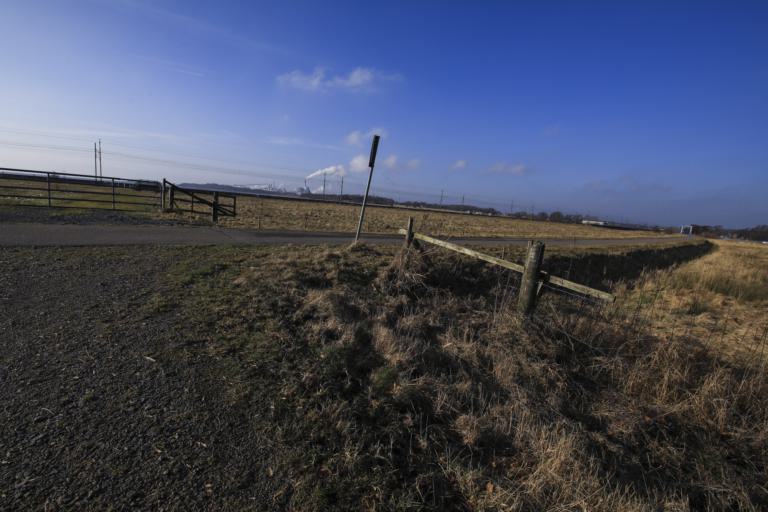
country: SE
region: Halland
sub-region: Kungsbacka Kommun
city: Frillesas
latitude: 57.2248
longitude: 12.2168
